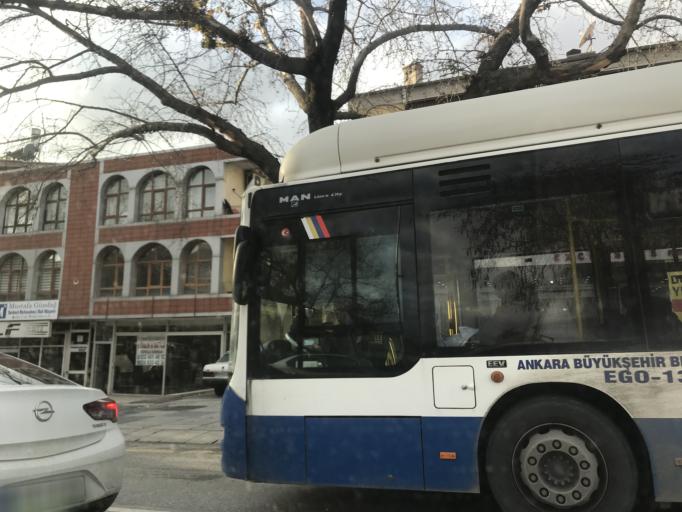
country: TR
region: Ankara
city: Mamak
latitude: 39.9662
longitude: 32.8733
